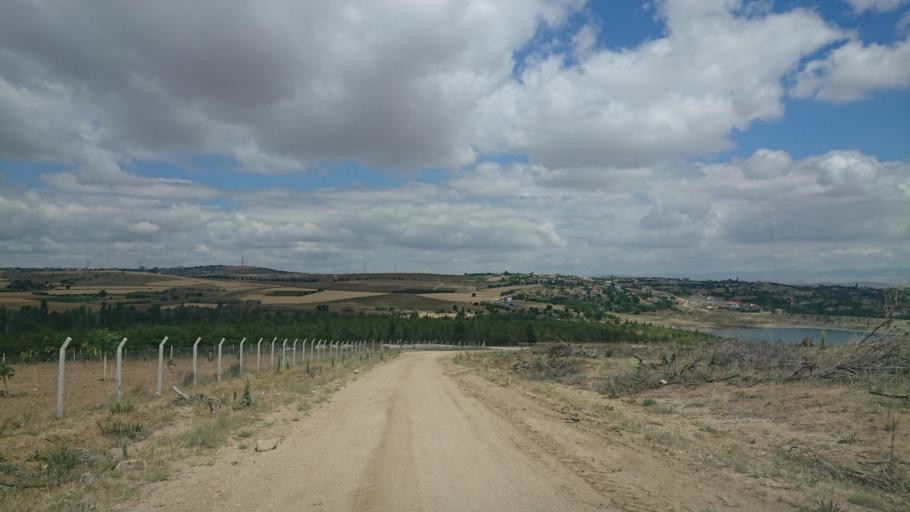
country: TR
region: Aksaray
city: Agacoren
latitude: 38.8583
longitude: 33.9483
